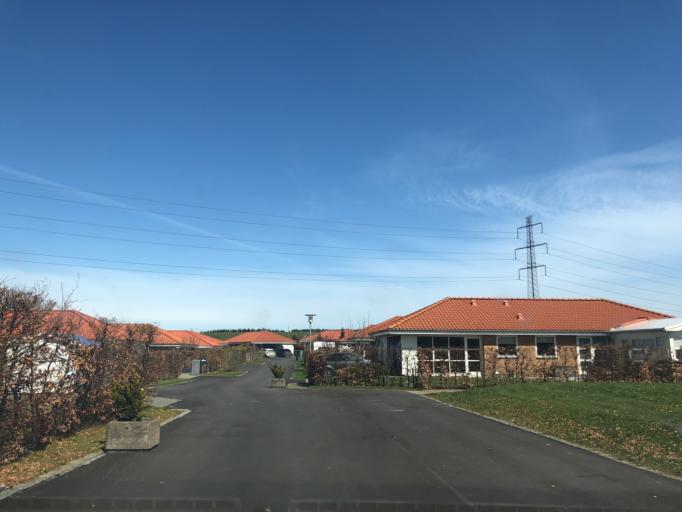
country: DK
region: Zealand
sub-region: Ringsted Kommune
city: Ringsted
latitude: 55.4542
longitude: 11.7706
